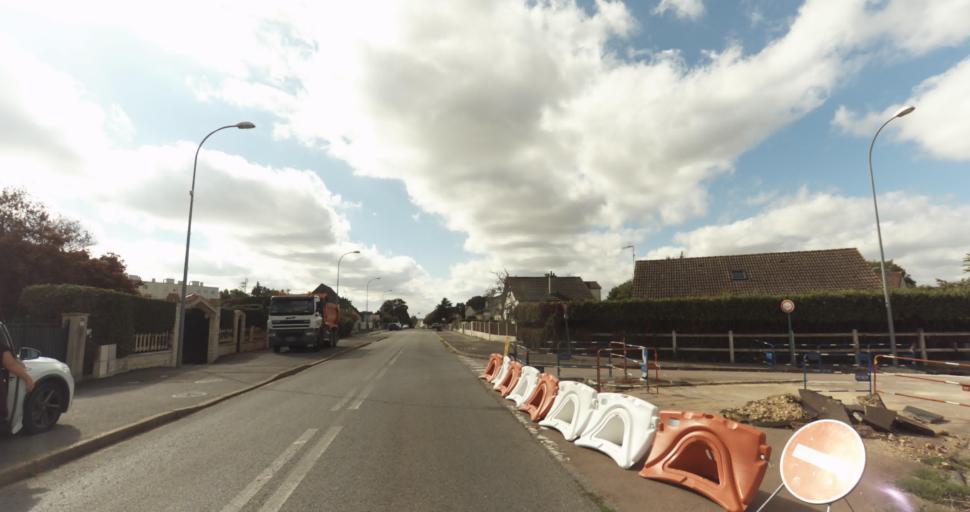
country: FR
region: Centre
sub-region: Departement d'Eure-et-Loir
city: Garnay
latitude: 48.7248
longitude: 1.3289
